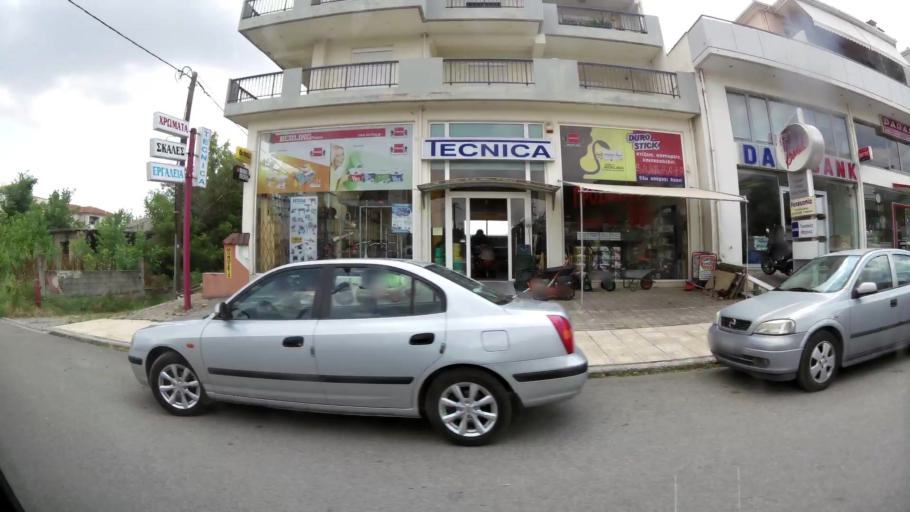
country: GR
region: West Macedonia
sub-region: Nomos Kozanis
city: Kozani
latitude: 40.2996
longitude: 21.8027
